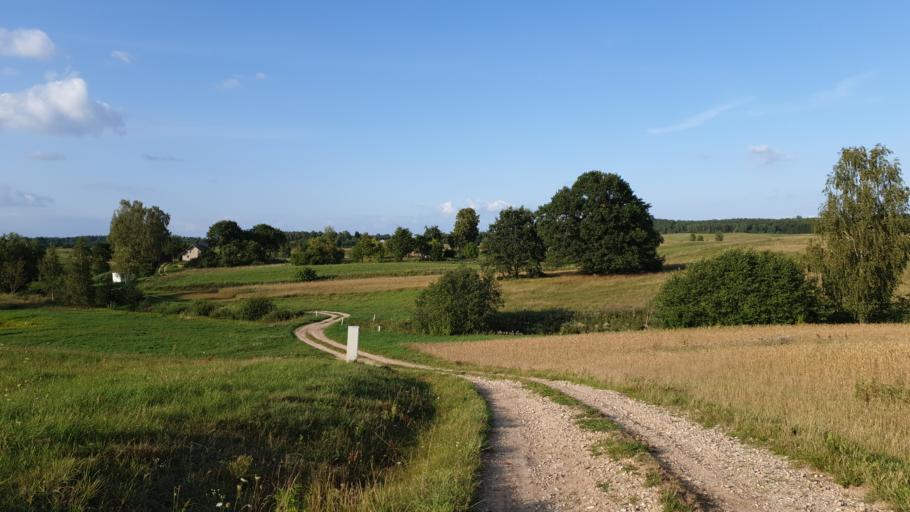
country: LT
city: Grigiskes
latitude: 54.7719
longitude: 25.0318
